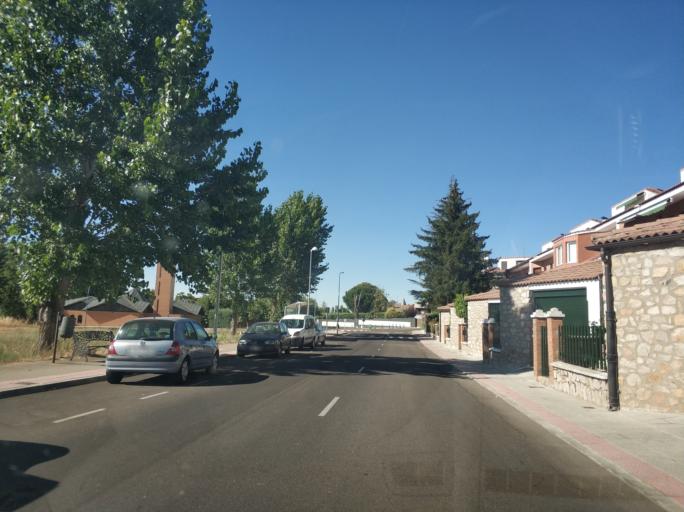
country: ES
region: Castille and Leon
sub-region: Provincia de Salamanca
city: Santa Marta de Tormes
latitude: 40.9365
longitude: -5.6252
